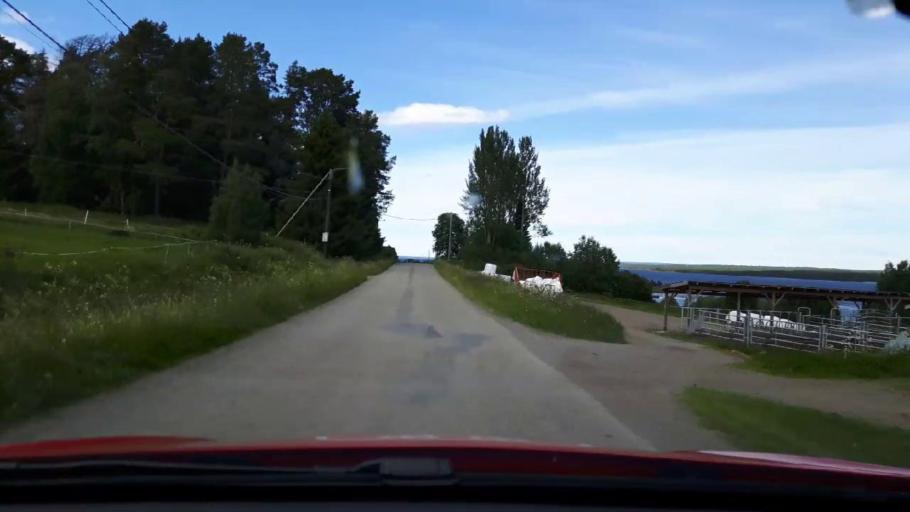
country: SE
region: Jaemtland
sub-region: Bergs Kommun
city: Hoverberg
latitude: 62.8228
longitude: 14.4606
